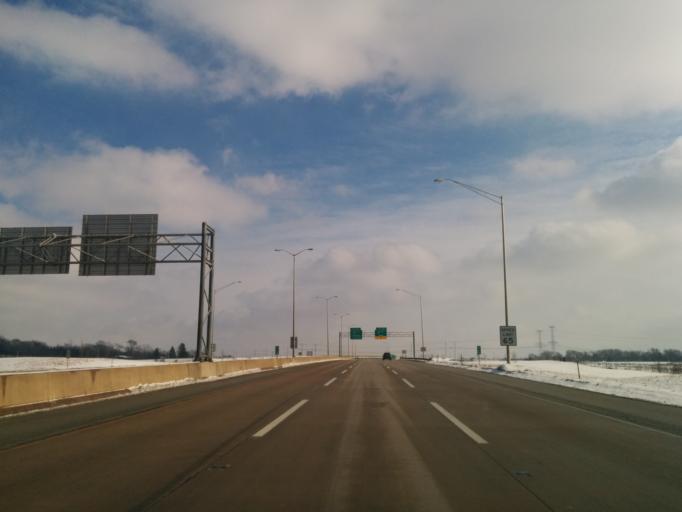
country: US
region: Illinois
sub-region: Will County
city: New Lenox
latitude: 41.5480
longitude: -87.9738
